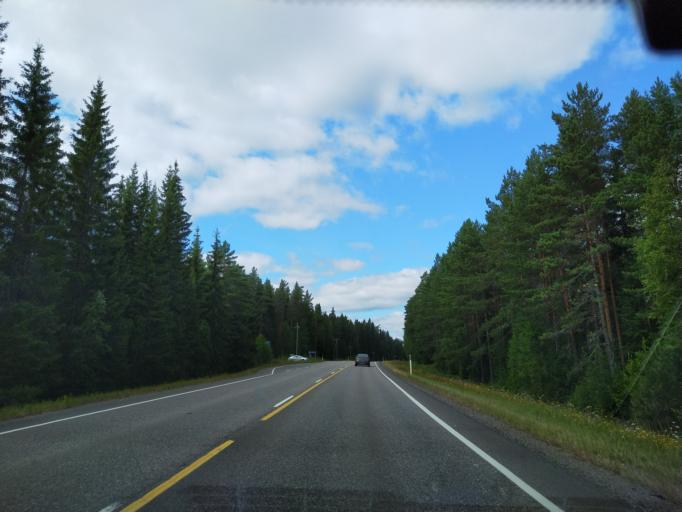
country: FI
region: Haeme
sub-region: Riihimaeki
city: Loppi
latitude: 60.7502
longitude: 24.3153
